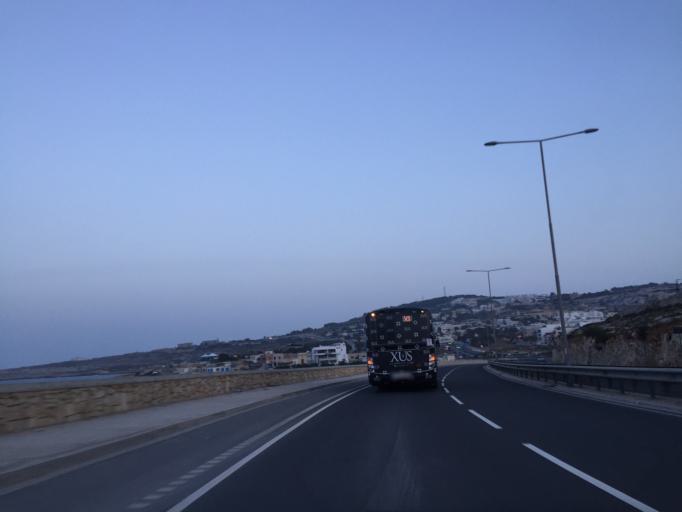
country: MT
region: Hal Gharghur
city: Hal Gharghur
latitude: 35.9427
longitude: 14.4537
